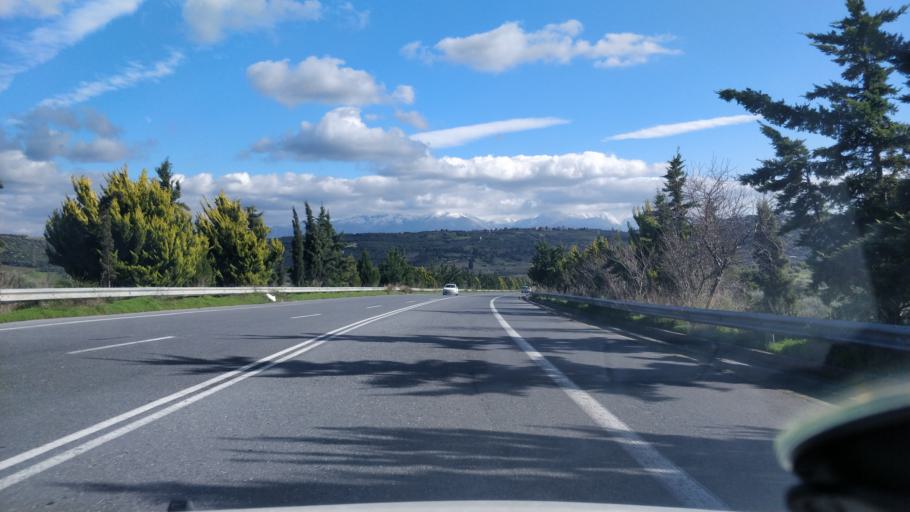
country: GR
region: Crete
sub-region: Nomos Irakleiou
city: Ano Arhanes
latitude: 35.2239
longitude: 25.1922
